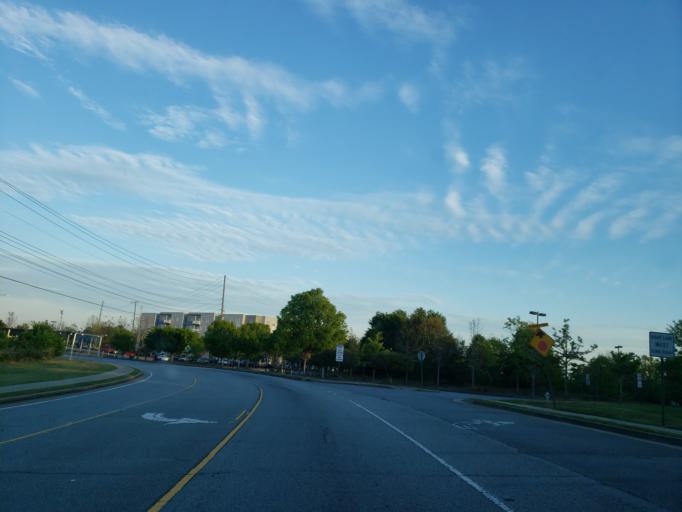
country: US
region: Georgia
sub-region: Cobb County
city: Kennesaw
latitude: 34.0298
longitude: -84.5717
